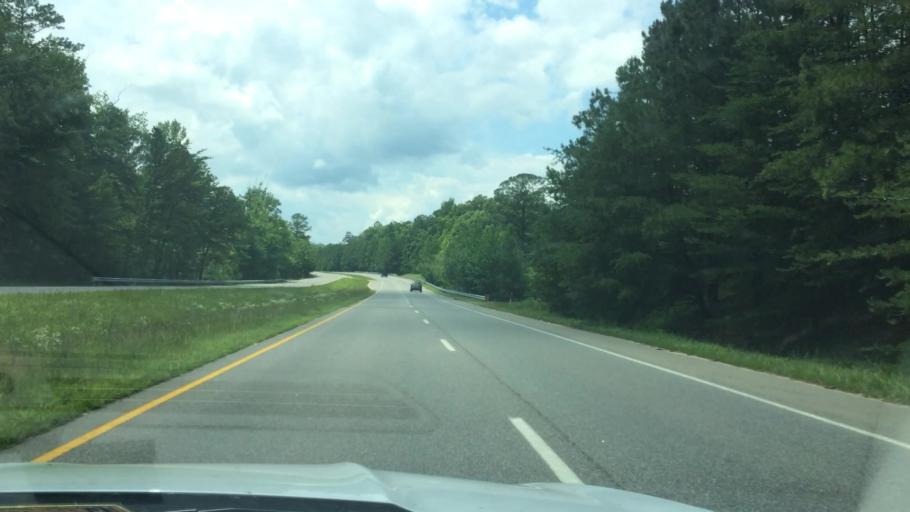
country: US
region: Virginia
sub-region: Middlesex County
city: Saluda
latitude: 37.5649
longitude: -76.6447
